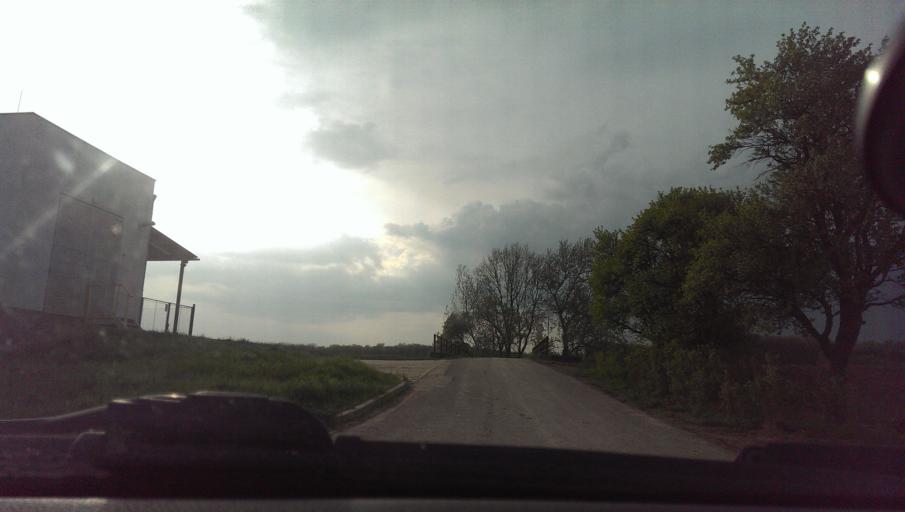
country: CZ
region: Zlin
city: Knezpole
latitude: 49.1042
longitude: 17.5062
